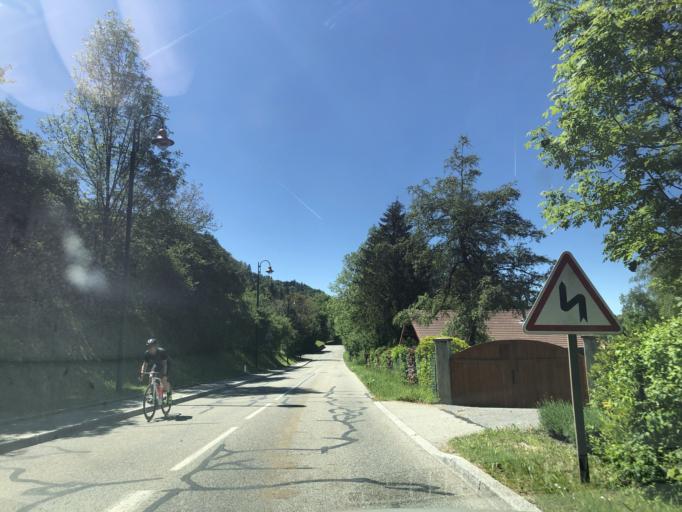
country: FR
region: Rhone-Alpes
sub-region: Departement de la Haute-Savoie
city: Menthon-Saint-Bernard
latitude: 45.8676
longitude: 6.2187
